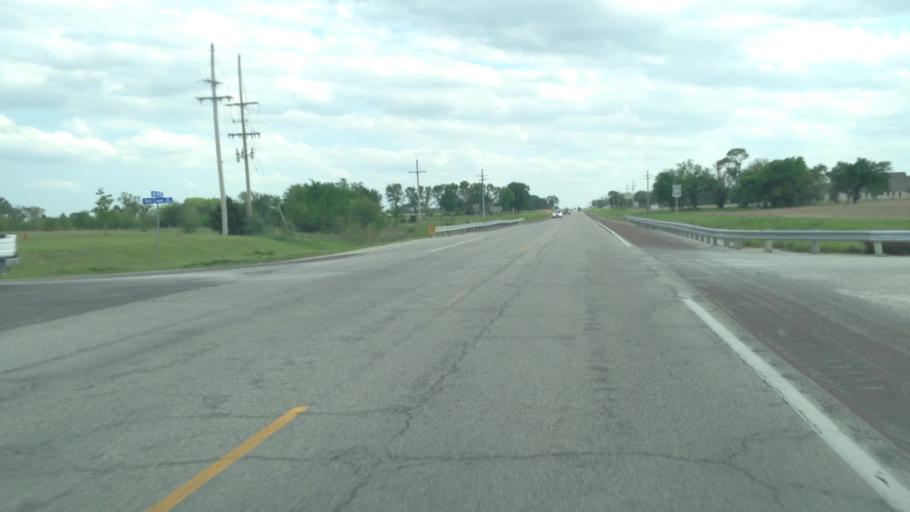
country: US
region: Kansas
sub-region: Franklin County
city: Ottawa
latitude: 38.5505
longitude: -95.2678
